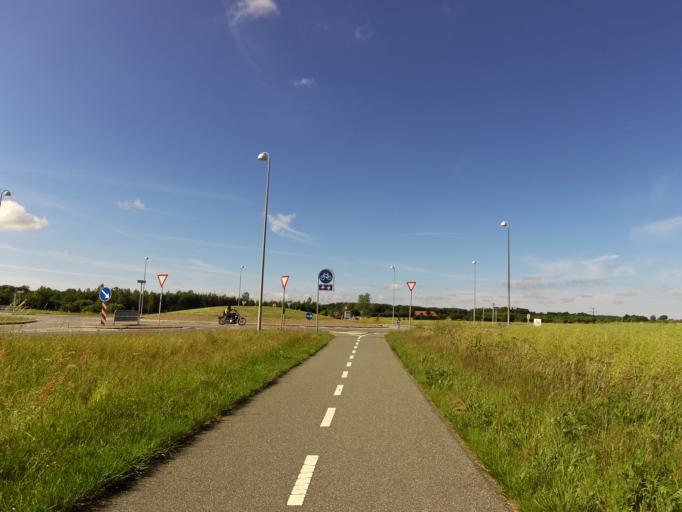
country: DK
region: South Denmark
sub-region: Aabenraa Kommune
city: Rodekro
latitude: 55.0762
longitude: 9.2207
